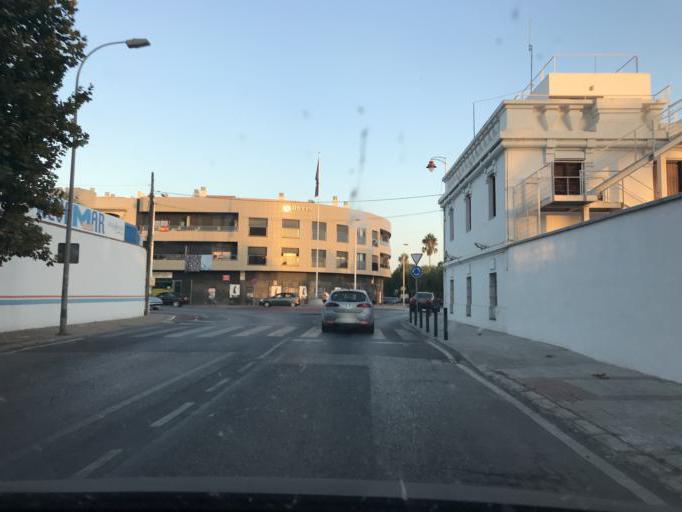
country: ES
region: Andalusia
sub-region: Provincia de Granada
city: El Varadero
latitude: 36.7249
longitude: -3.5258
